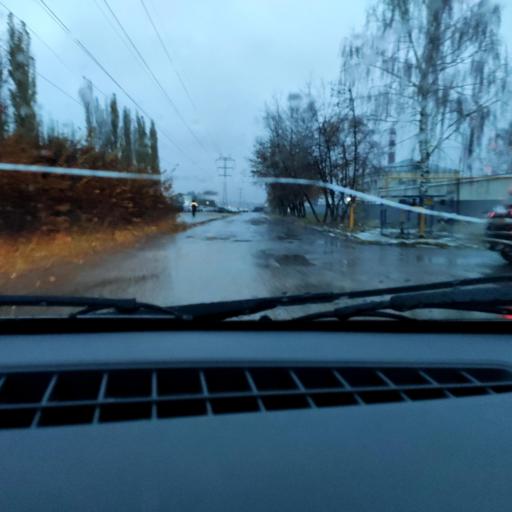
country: RU
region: Bashkortostan
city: Avdon
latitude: 54.6831
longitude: 55.8018
